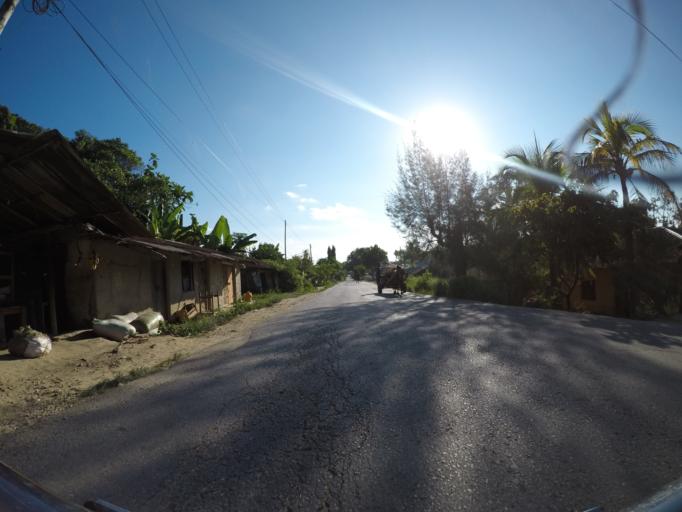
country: TZ
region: Pemba South
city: Chake Chake
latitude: -5.2968
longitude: 39.7591
